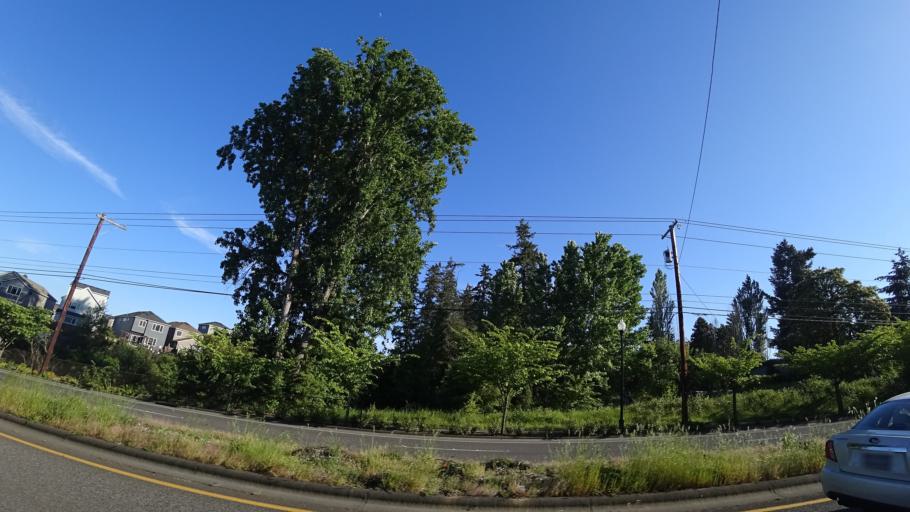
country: US
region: Oregon
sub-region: Washington County
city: Aloha
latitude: 45.5153
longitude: -122.8925
